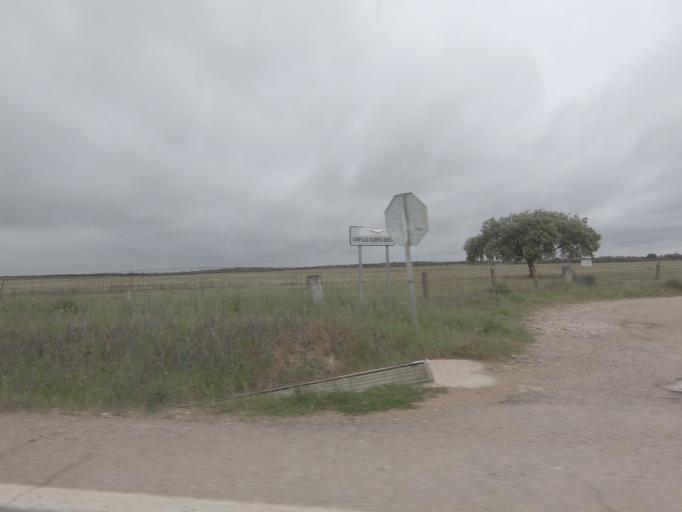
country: ES
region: Extremadura
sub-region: Provincia de Badajoz
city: Badajoz
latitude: 38.9752
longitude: -6.8893
